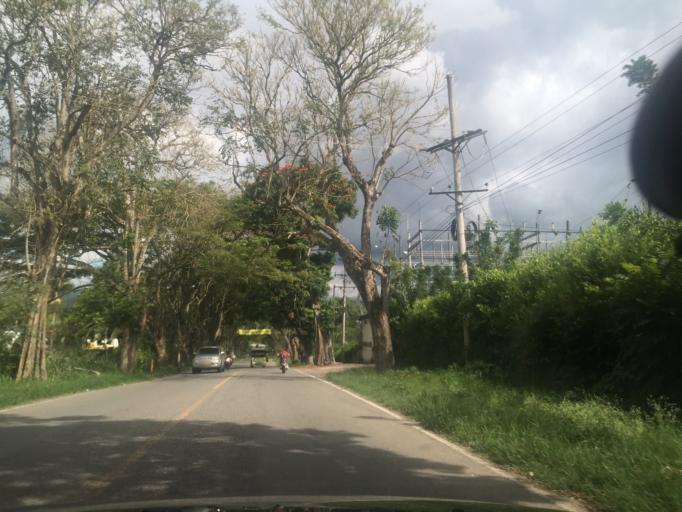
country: CO
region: Valle del Cauca
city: Caicedonia
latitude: 4.3415
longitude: -75.8343
